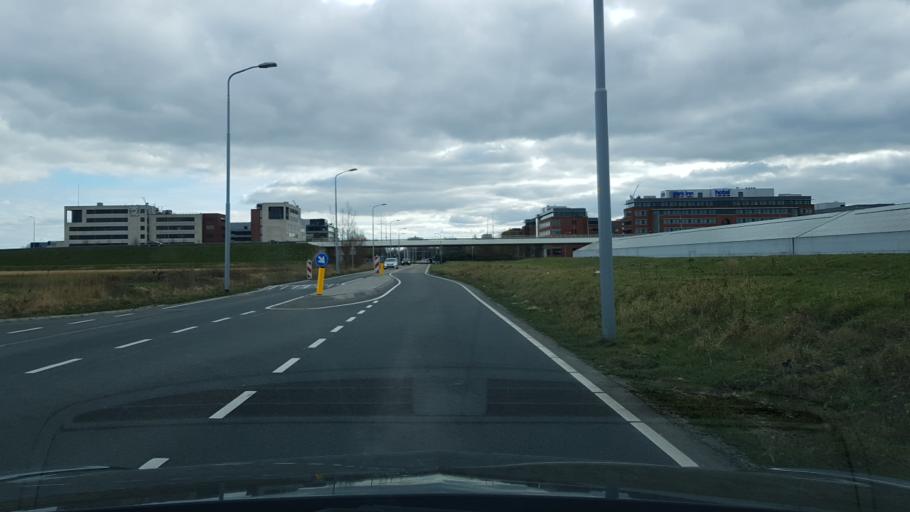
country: NL
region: North Holland
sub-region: Gemeente Aalsmeer
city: Aalsmeer
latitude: 52.2817
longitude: 4.7421
